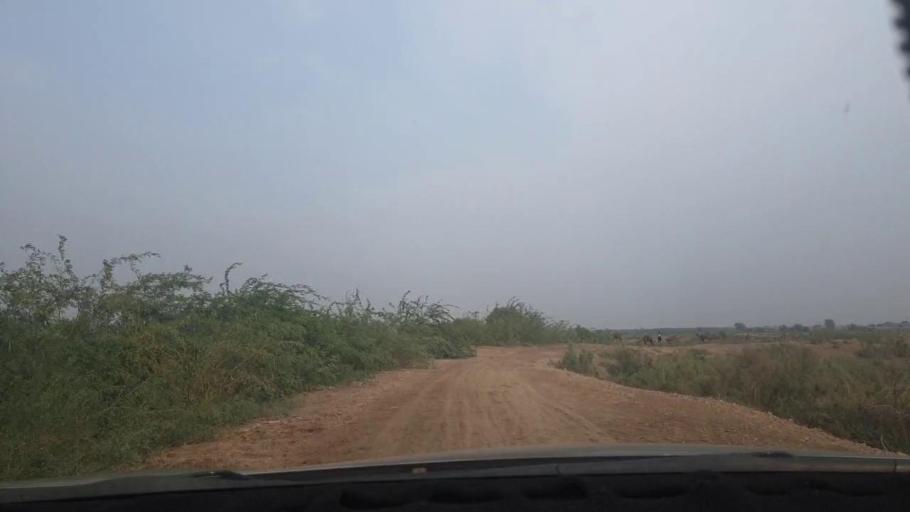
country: PK
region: Sindh
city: Jamshoro
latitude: 25.5212
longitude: 68.3180
